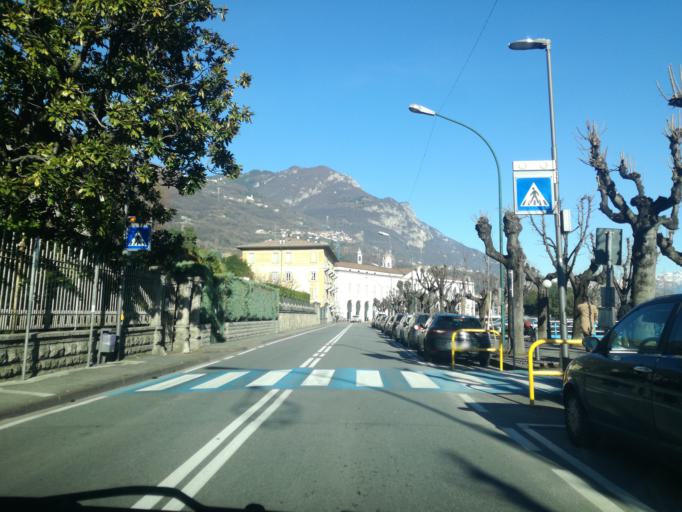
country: IT
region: Lombardy
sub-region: Provincia di Bergamo
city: Lovere
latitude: 45.8132
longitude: 10.0719
